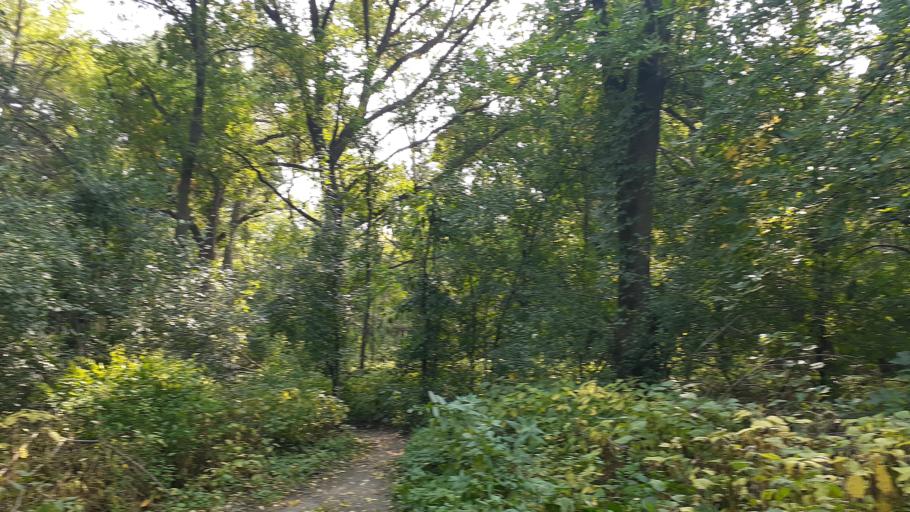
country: US
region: Minnesota
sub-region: Clay County
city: Oakport
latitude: 46.9110
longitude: -96.7618
